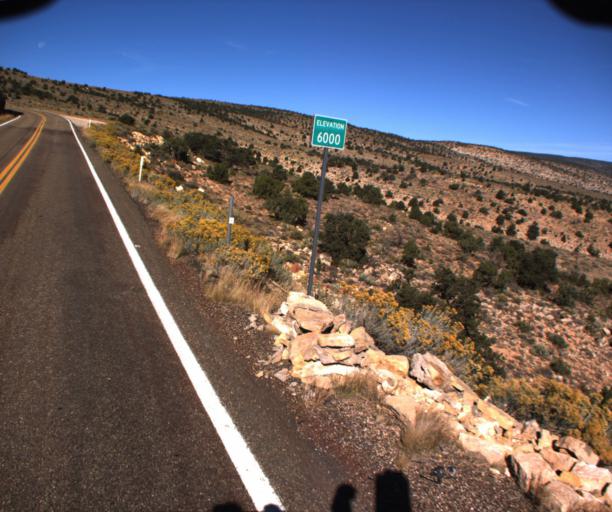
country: US
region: Arizona
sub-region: Coconino County
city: Fredonia
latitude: 36.7263
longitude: -112.0658
